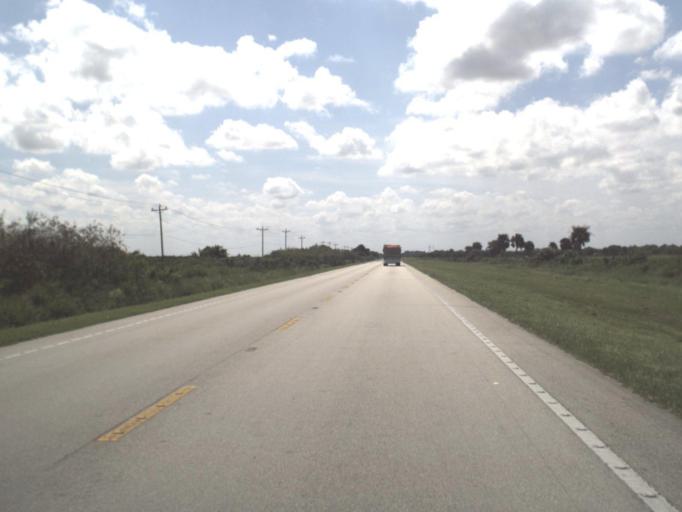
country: US
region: Florida
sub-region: Collier County
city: Immokalee
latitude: 26.5015
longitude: -81.4349
